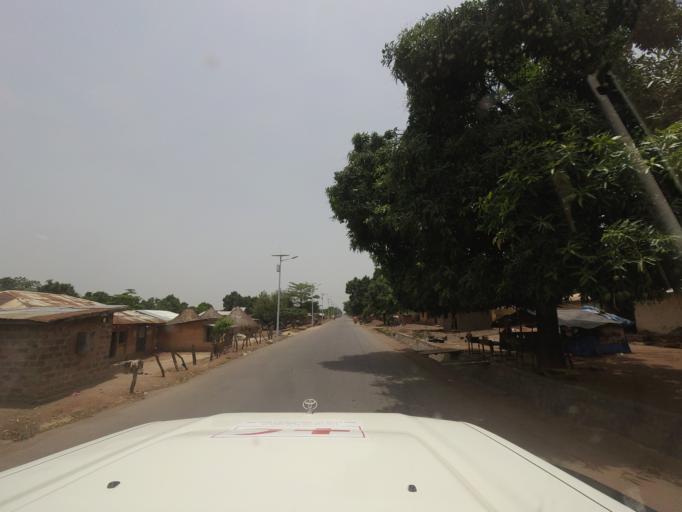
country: GN
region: Faranah
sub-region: Faranah Prefecture
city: Faranah
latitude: 9.7345
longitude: -10.6350
